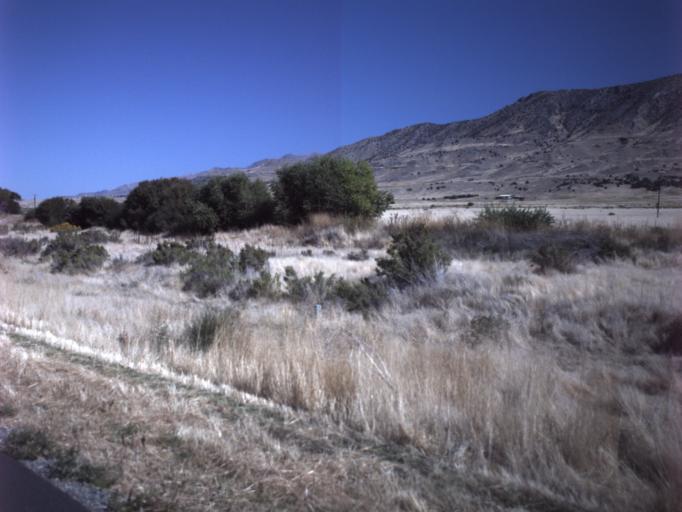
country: US
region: Utah
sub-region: Tooele County
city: Grantsville
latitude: 40.5327
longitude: -112.7477
